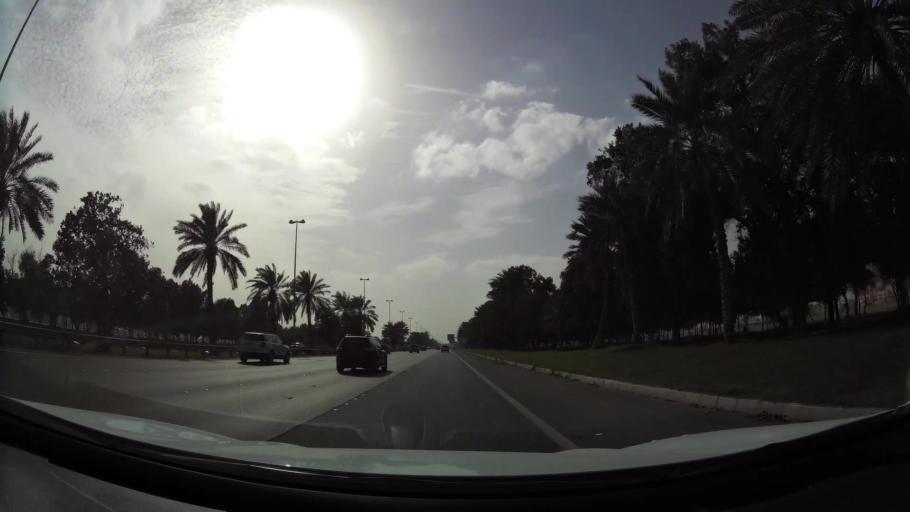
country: AE
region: Abu Dhabi
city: Abu Dhabi
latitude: 24.3999
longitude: 54.5845
